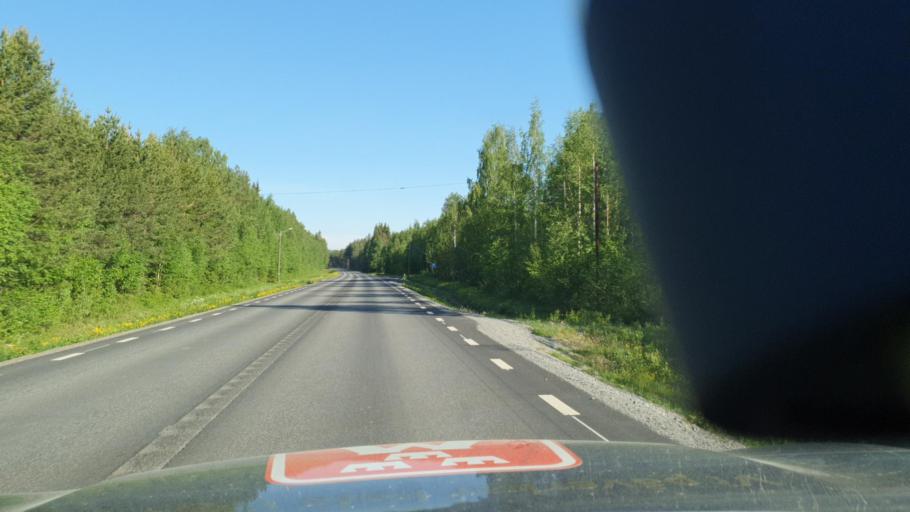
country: SE
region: Norrbotten
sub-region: Alvsbyns Kommun
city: AElvsbyn
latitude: 66.1301
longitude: 20.9081
